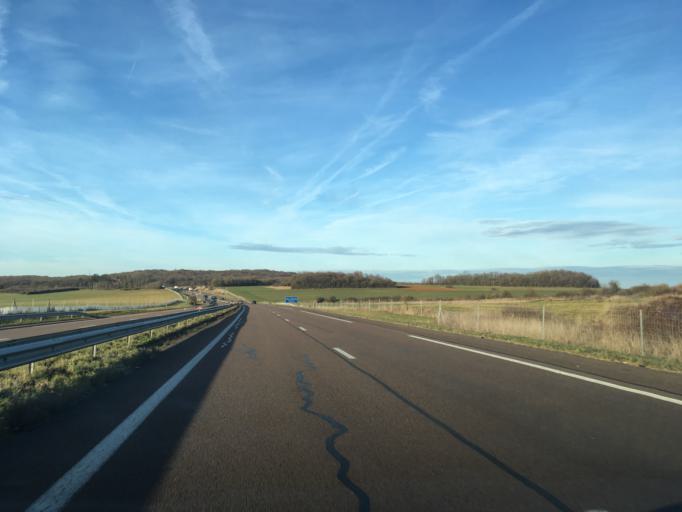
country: FR
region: Bourgogne
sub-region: Departement de l'Yonne
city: Joux-la-Ville
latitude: 47.5716
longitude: 3.9378
